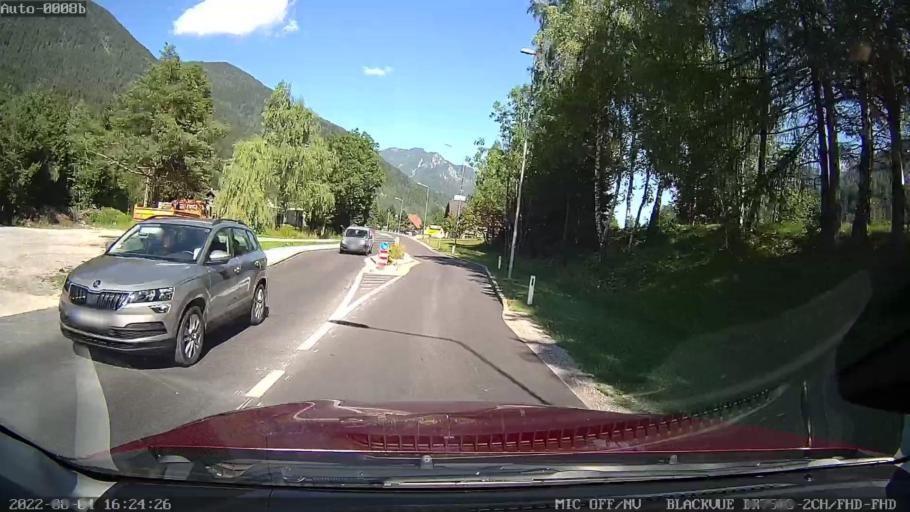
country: SI
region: Kranjska Gora
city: Kranjska Gora
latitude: 46.4863
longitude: 13.8032
